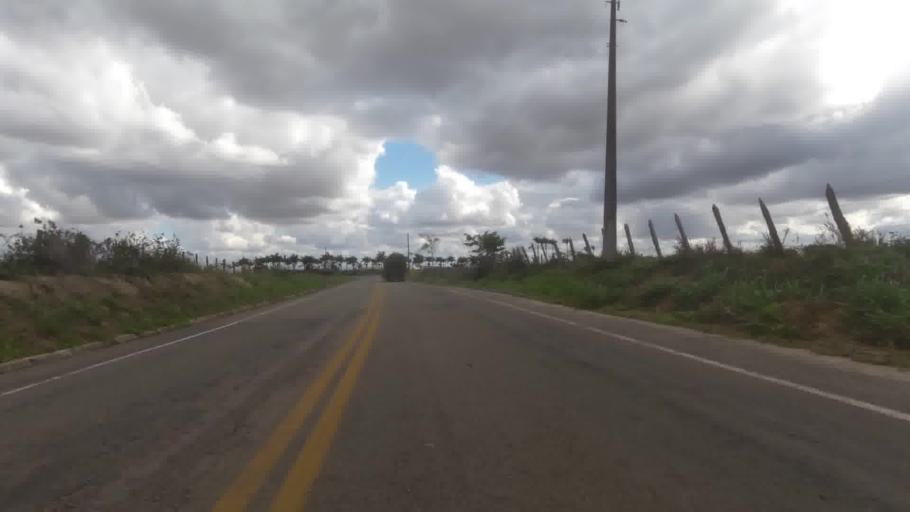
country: BR
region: Espirito Santo
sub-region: Marataizes
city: Marataizes
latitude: -21.1880
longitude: -40.9747
